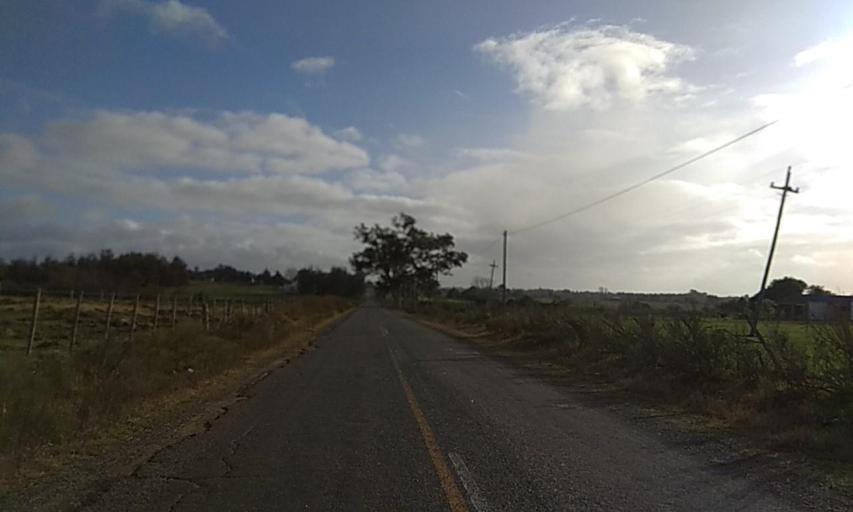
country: UY
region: Florida
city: Florida
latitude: -34.0526
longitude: -56.1897
